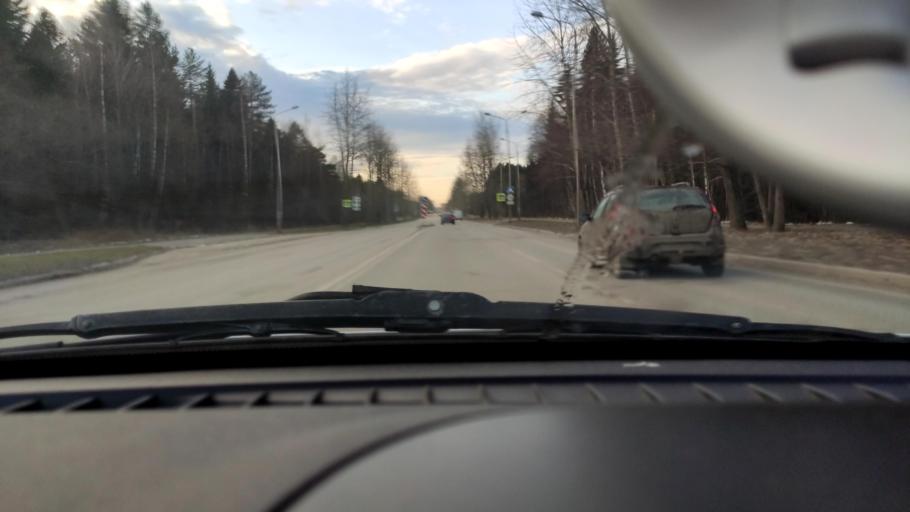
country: RU
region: Perm
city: Perm
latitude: 58.0868
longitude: 56.3791
